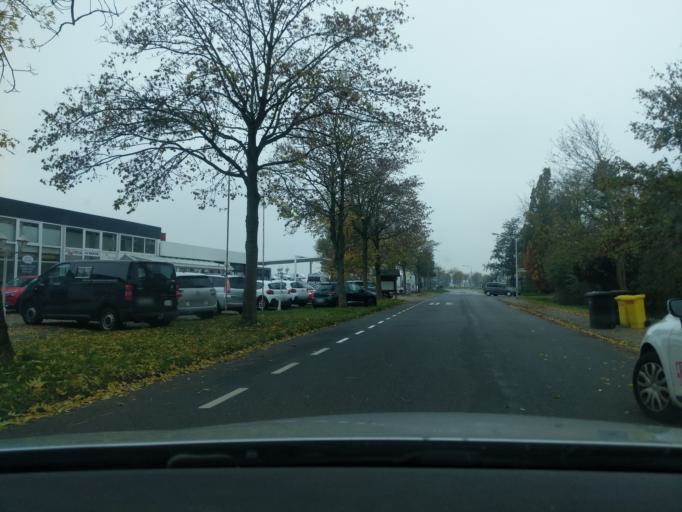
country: DE
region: Lower Saxony
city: Wanna
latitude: 53.8261
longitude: 8.7648
